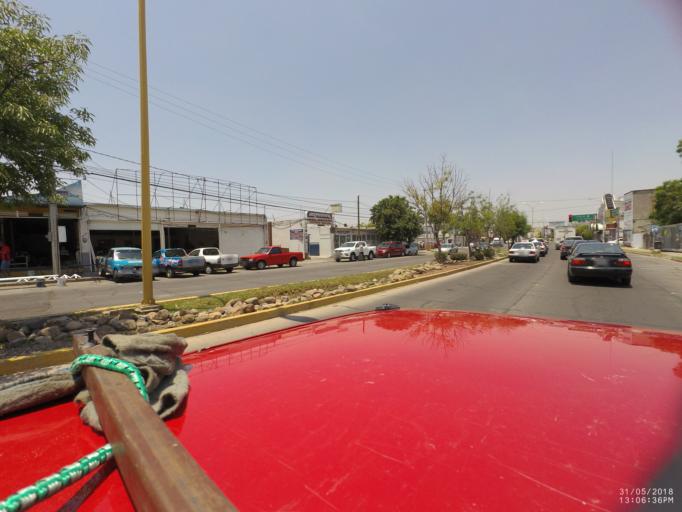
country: MX
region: Aguascalientes
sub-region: Aguascalientes
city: Aguascalientes
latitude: 21.8735
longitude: -102.2881
